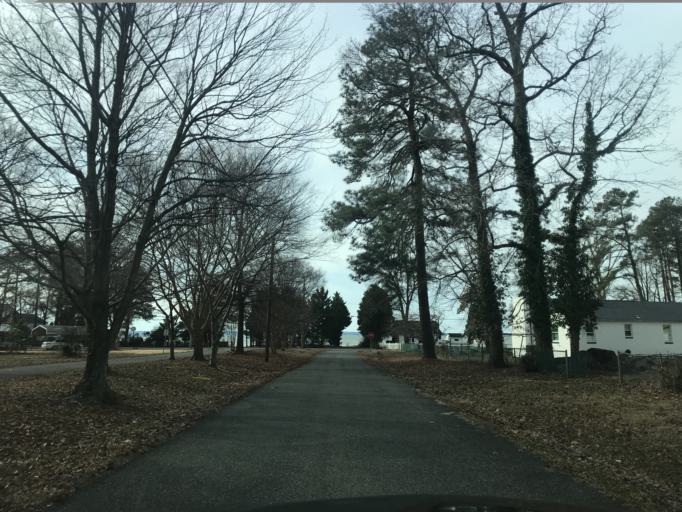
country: US
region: Maryland
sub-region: Charles County
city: Cobb Island
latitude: 38.2617
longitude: -76.8509
